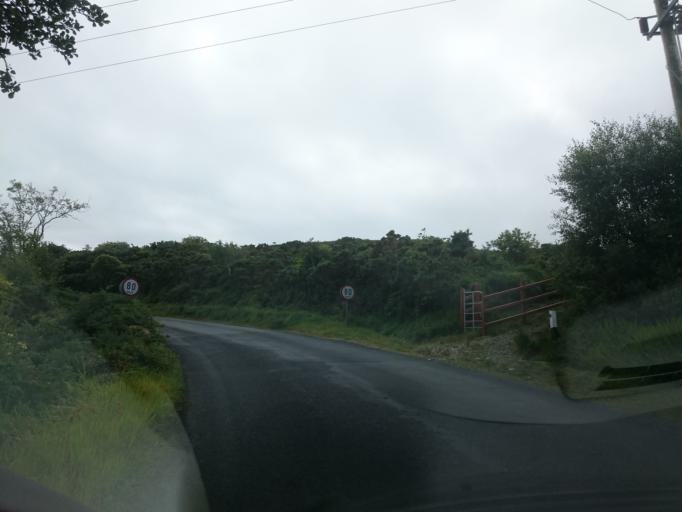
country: IE
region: Connaught
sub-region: Maigh Eo
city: Westport
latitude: 53.9052
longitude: -9.7898
